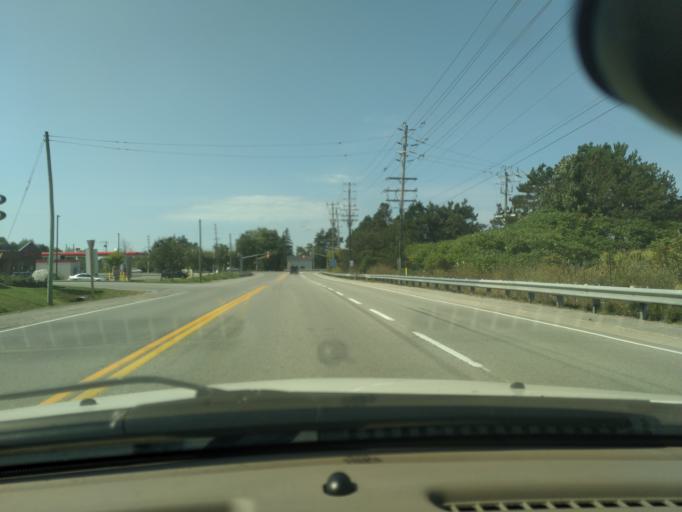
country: CA
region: Ontario
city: Innisfil
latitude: 44.2758
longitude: -79.7210
